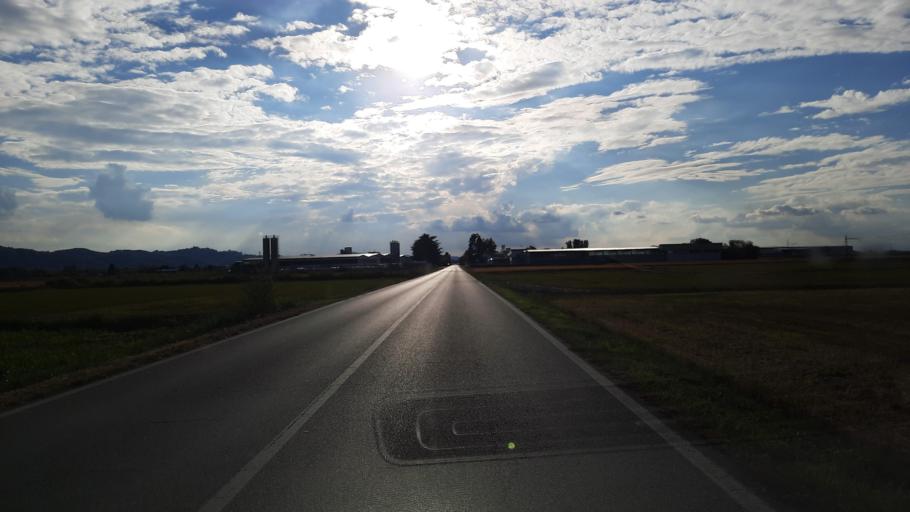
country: IT
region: Piedmont
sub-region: Provincia di Vercelli
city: Palazzolo Vercellese
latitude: 45.1896
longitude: 8.2463
